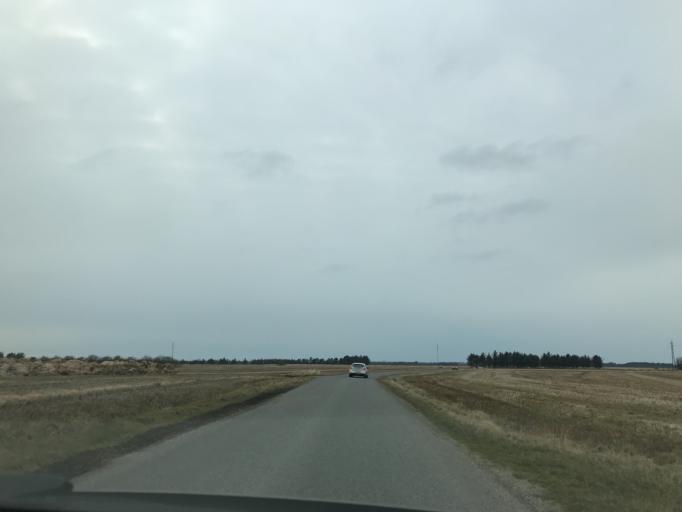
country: DK
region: South Denmark
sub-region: Varde Kommune
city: Oksbol
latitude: 55.8173
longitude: 8.2843
